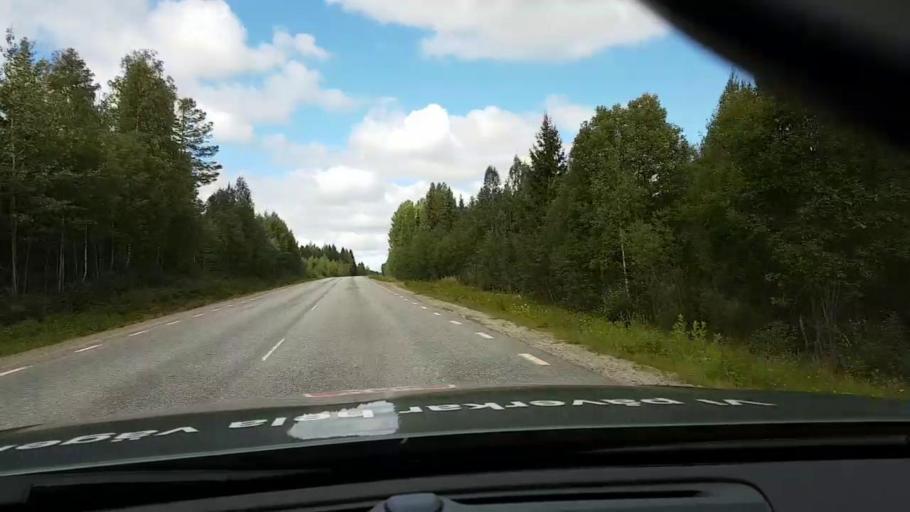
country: SE
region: Vaesternorrland
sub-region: OErnskoeldsviks Kommun
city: Bredbyn
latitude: 63.4712
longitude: 18.0994
